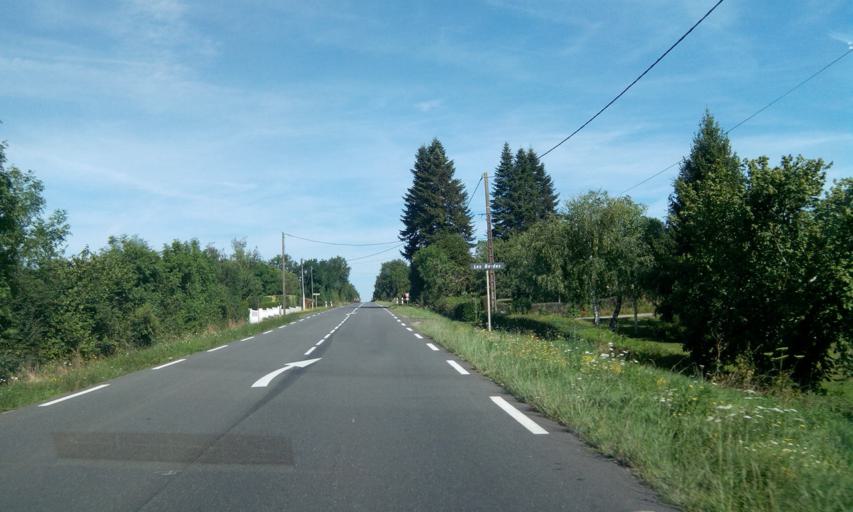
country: FR
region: Poitou-Charentes
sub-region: Departement de la Charente
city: Etagnac
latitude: 45.9404
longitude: 0.7301
